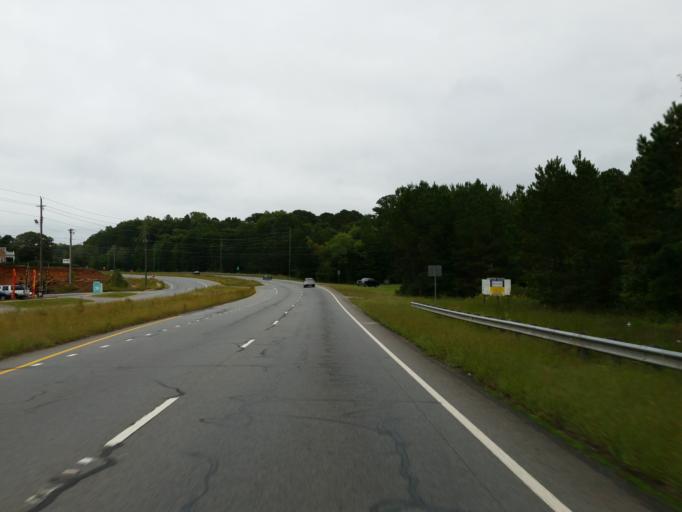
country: US
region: Georgia
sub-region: Cherokee County
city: Woodstock
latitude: 34.0777
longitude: -84.4406
